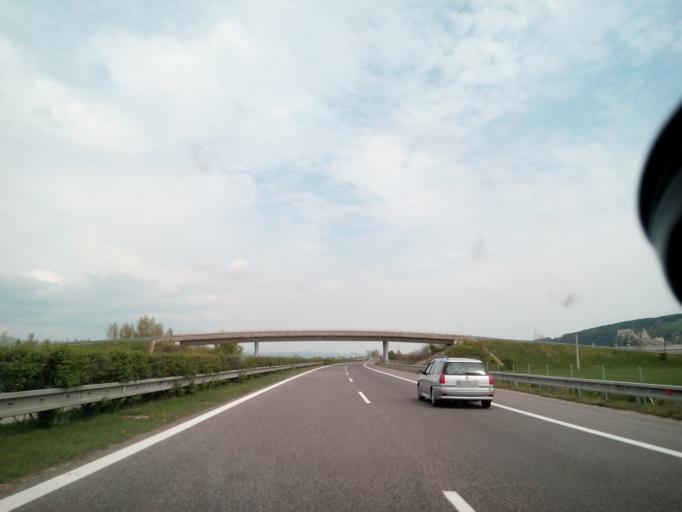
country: SK
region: Trenciansky
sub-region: Okres Nove Mesto nad Vahom
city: Nove Mesto nad Vahom
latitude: 48.7829
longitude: 17.8812
